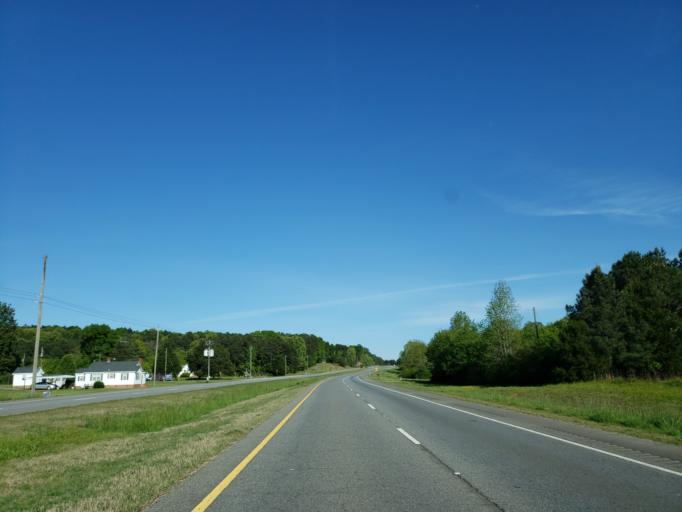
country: US
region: Georgia
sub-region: Polk County
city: Cedartown
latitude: 34.0134
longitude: -85.1883
